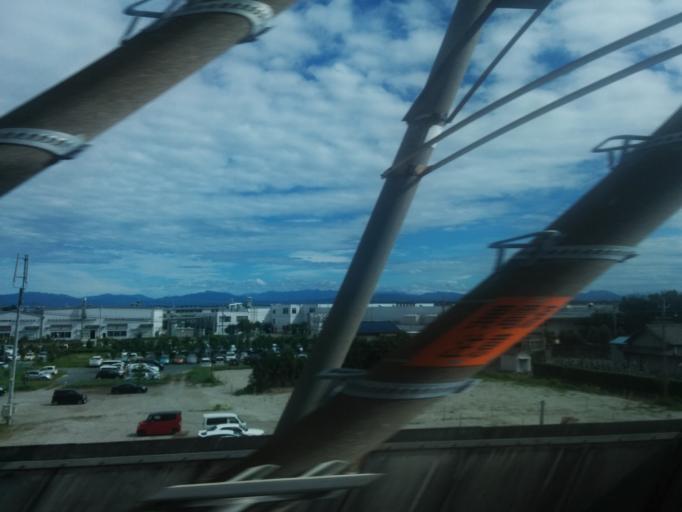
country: JP
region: Shizuoka
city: Iwata
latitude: 34.7076
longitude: 137.7926
